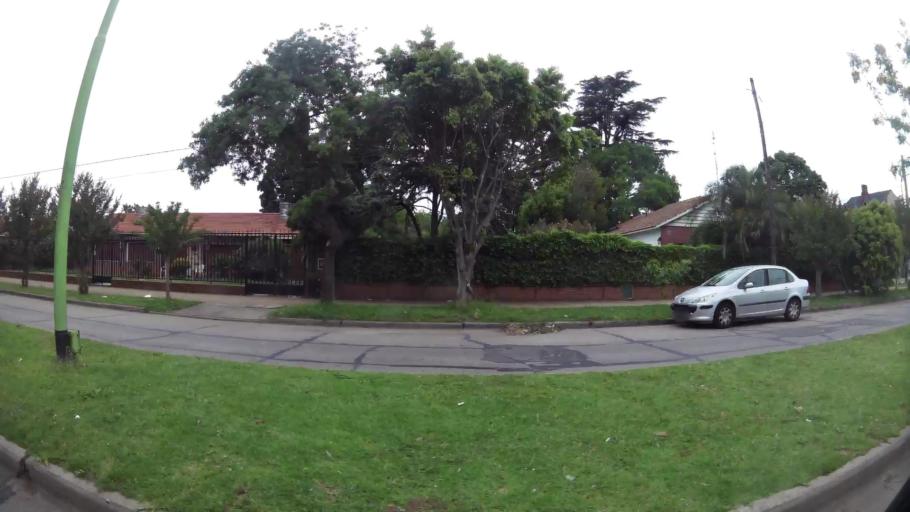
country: AR
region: Buenos Aires
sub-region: Partido de Campana
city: Campana
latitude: -34.1757
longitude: -58.9600
